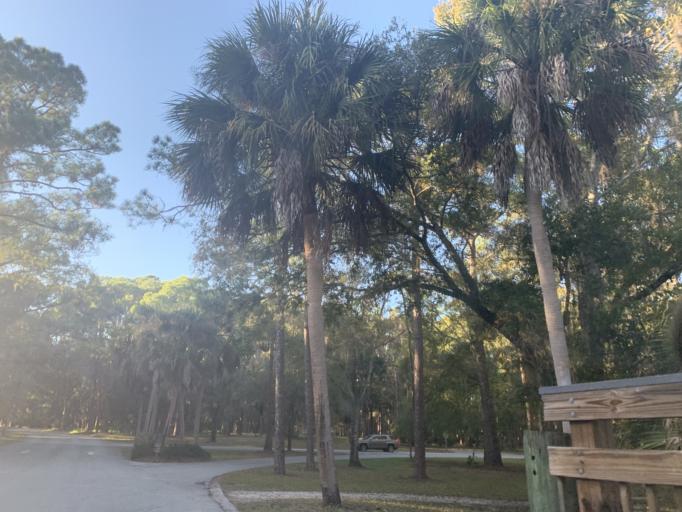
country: US
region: Florida
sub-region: Pinellas County
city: East Lake
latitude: 28.0927
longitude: -82.7066
